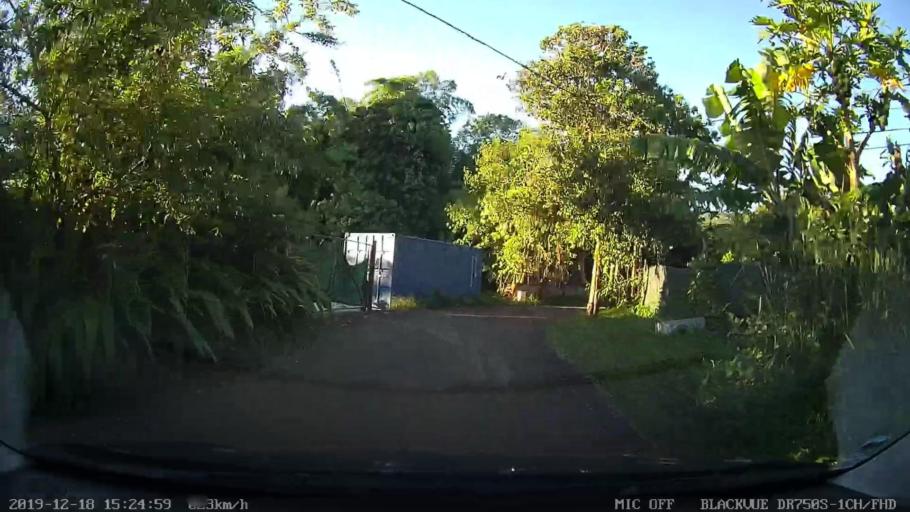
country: RE
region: Reunion
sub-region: Reunion
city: Bras-Panon
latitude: -21.0016
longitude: 55.6531
